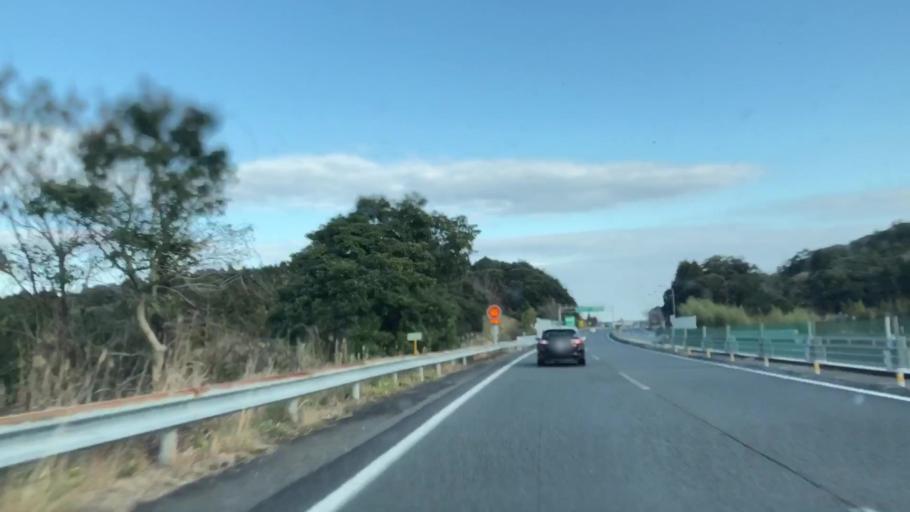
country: JP
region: Miyazaki
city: Miyazaki-shi
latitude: 31.8672
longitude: 131.3914
